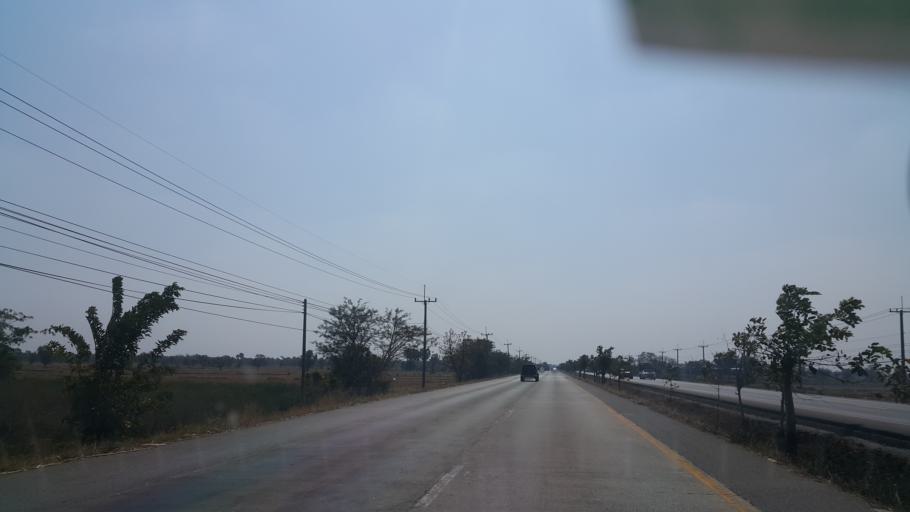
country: TH
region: Nakhon Ratchasima
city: Non Daeng
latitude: 15.4820
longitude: 102.5169
